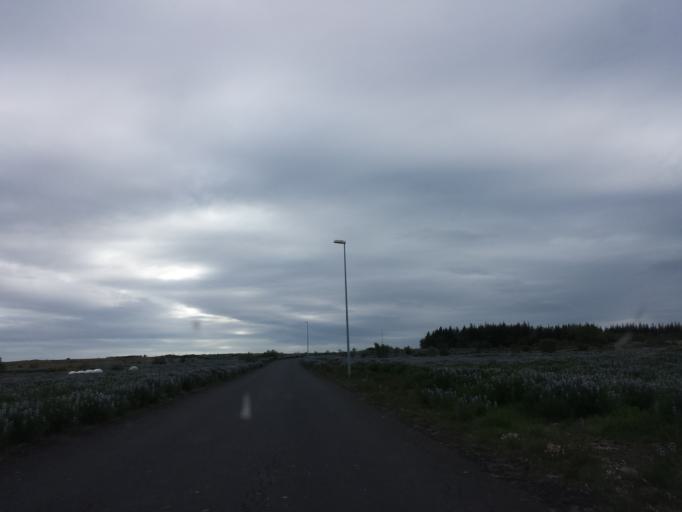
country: IS
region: Capital Region
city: Alftanes
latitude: 64.0885
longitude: -21.9830
